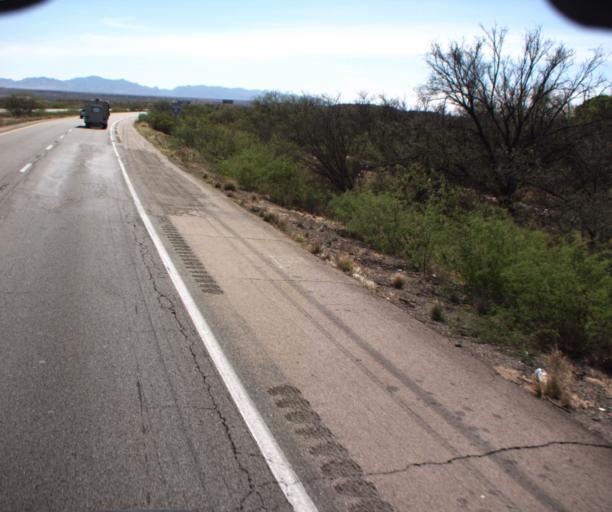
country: US
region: Arizona
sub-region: Cochise County
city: Benson
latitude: 31.9784
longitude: -110.2976
